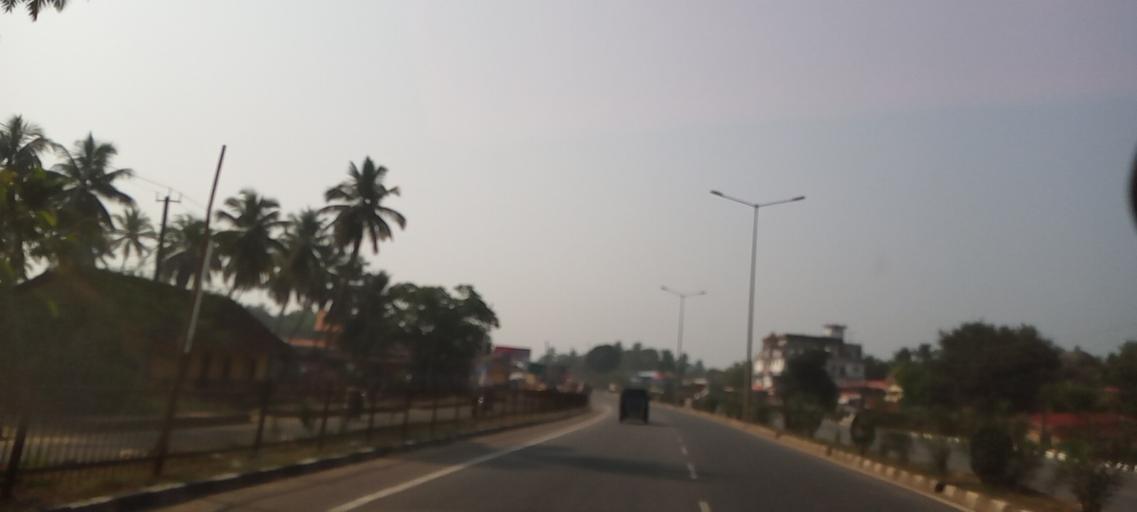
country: IN
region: Karnataka
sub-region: Udupi
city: Coondapoor
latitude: 13.5223
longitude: 74.7059
